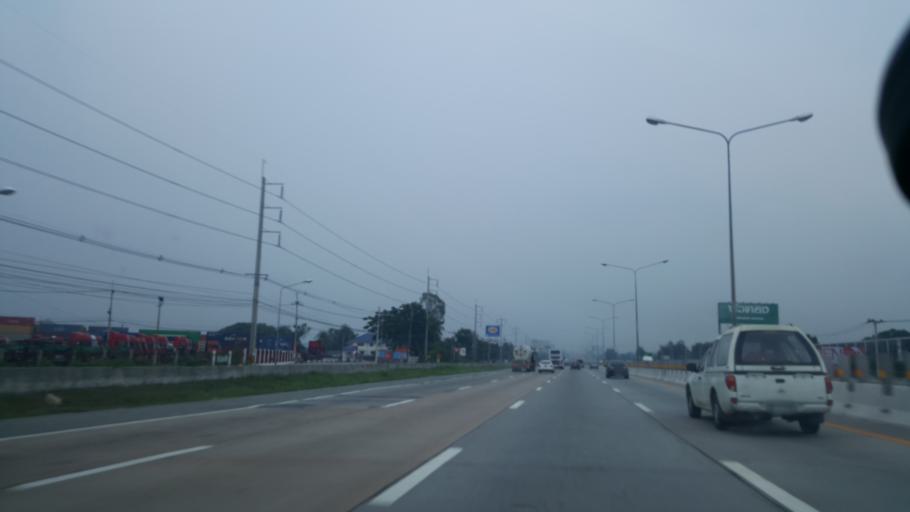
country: TH
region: Chon Buri
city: Si Racha
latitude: 13.1920
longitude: 100.9991
